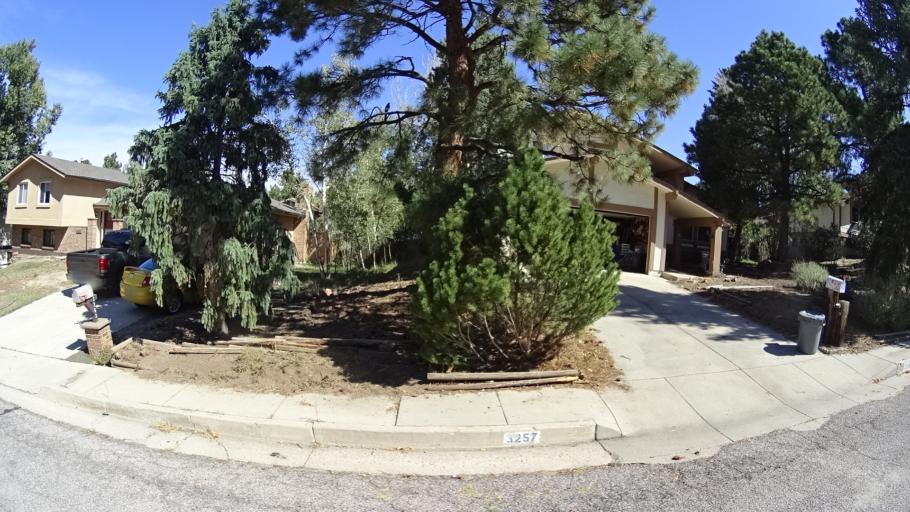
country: US
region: Colorado
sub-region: El Paso County
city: Cimarron Hills
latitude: 38.9129
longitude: -104.7685
